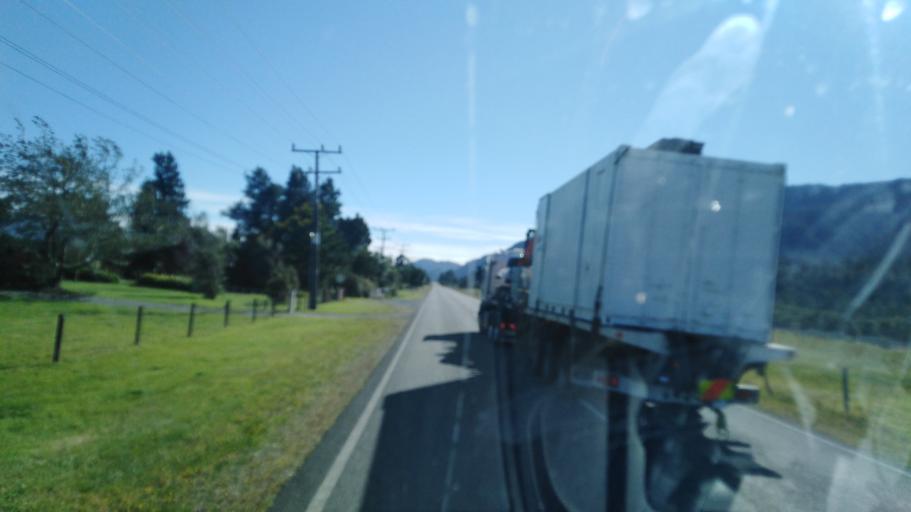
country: NZ
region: West Coast
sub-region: Buller District
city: Westport
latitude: -41.6755
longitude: 171.7990
